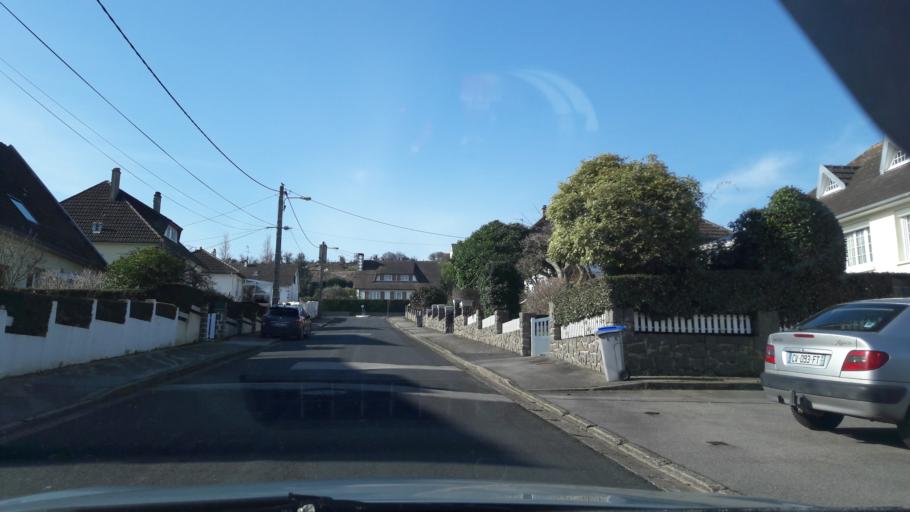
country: FR
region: Lower Normandy
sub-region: Departement de la Manche
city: Querqueville
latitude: 49.6556
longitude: -1.6849
